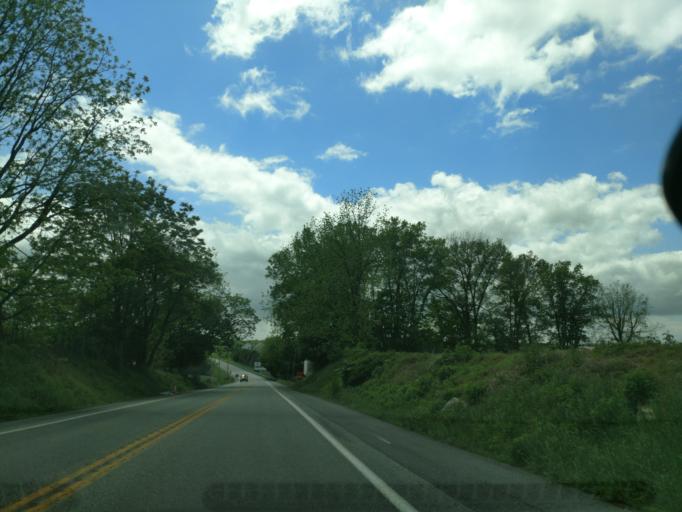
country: US
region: Pennsylvania
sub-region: Lebanon County
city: Lebanon South
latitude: 40.3012
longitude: -76.4240
